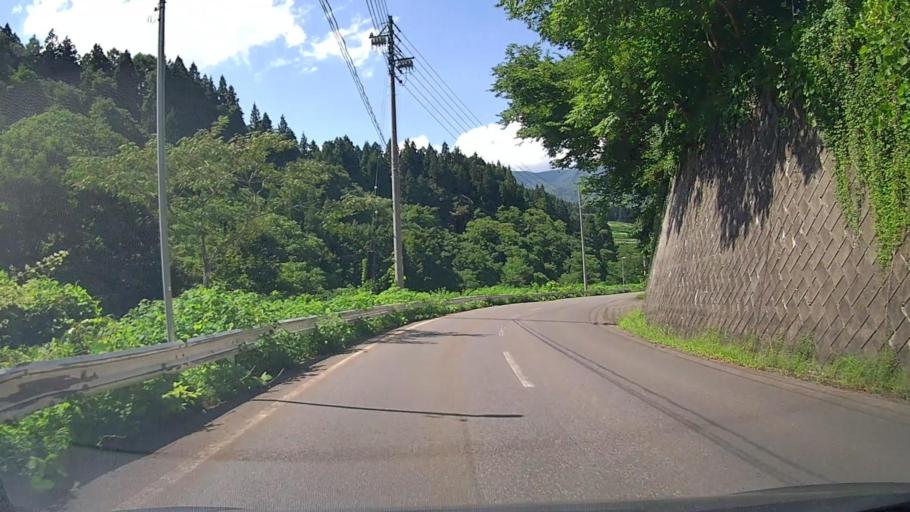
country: JP
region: Nagano
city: Iiyama
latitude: 36.9257
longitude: 138.4247
